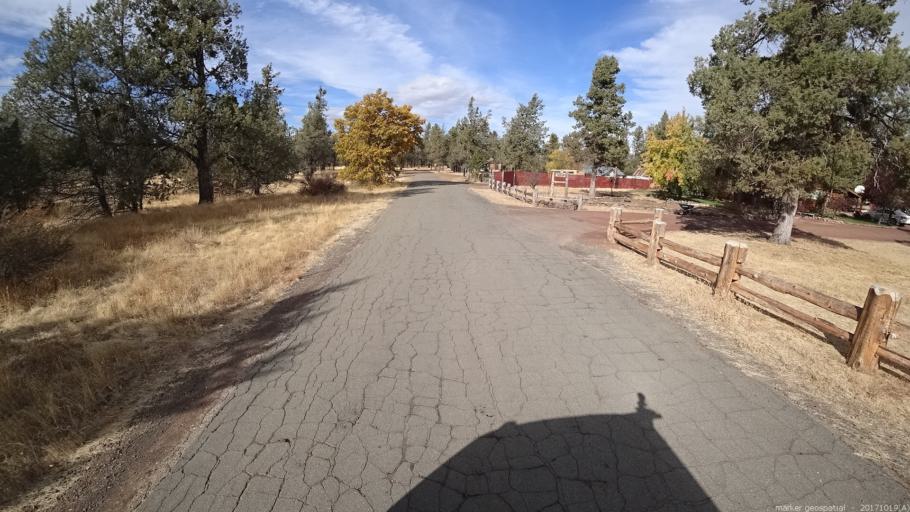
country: US
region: California
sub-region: Shasta County
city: Burney
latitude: 41.0033
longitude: -121.4465
